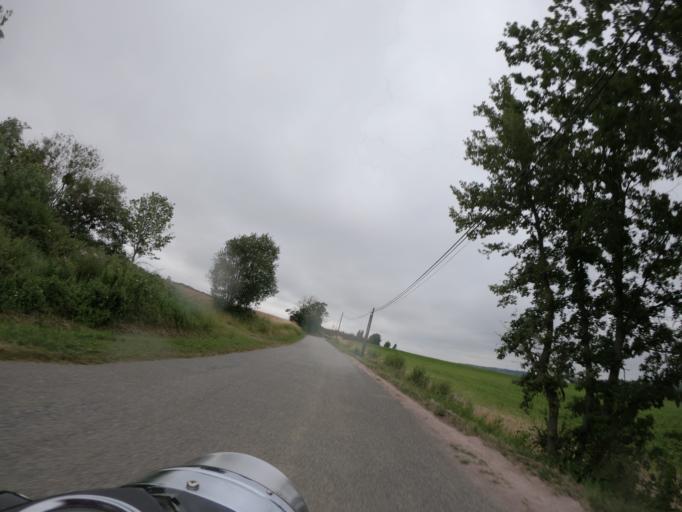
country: FR
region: Midi-Pyrenees
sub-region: Departement de l'Ariege
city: La Tour-du-Crieu
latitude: 43.0976
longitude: 1.7212
